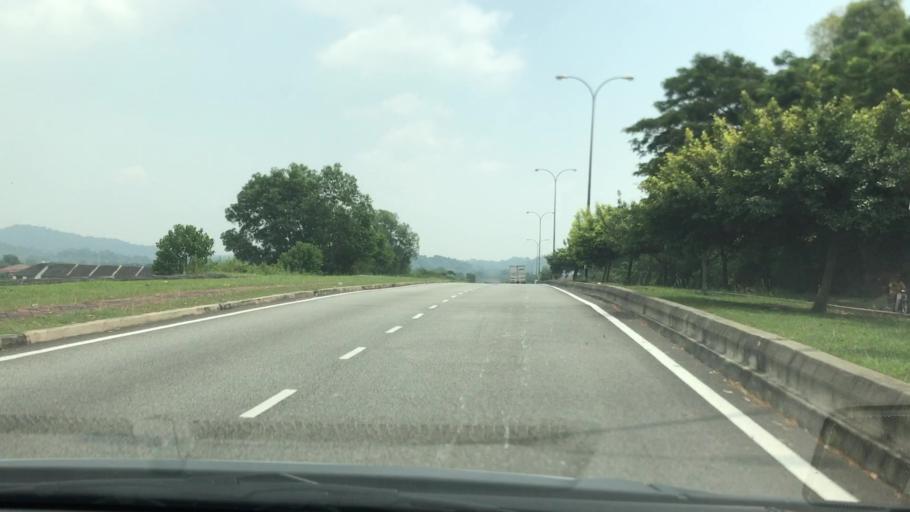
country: MY
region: Putrajaya
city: Putrajaya
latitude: 2.9892
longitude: 101.6641
